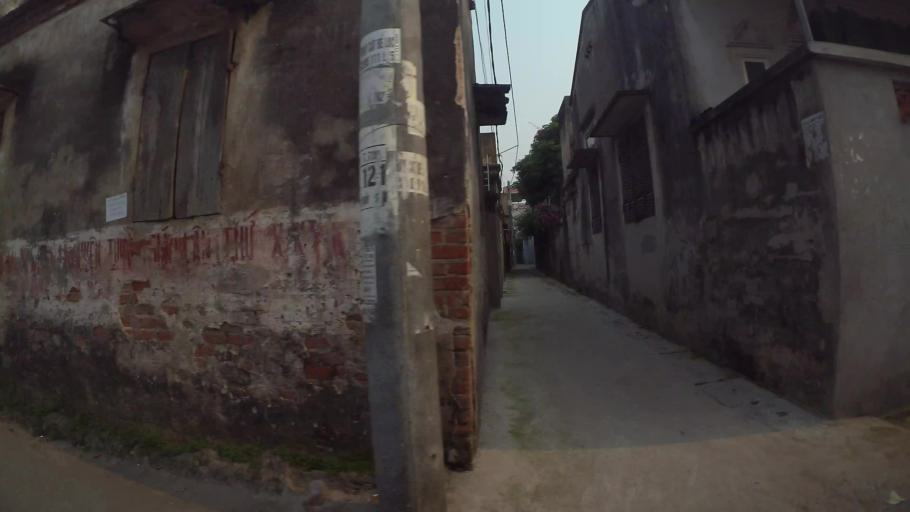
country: VN
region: Ha Noi
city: Thuong Tin
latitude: 20.8655
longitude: 105.8767
